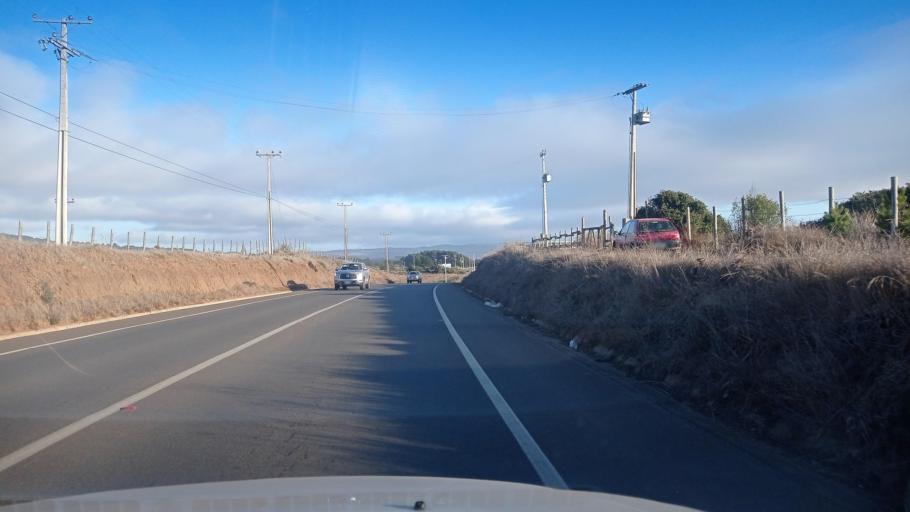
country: CL
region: O'Higgins
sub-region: Provincia de Colchagua
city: Santa Cruz
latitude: -34.4436
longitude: -72.0323
